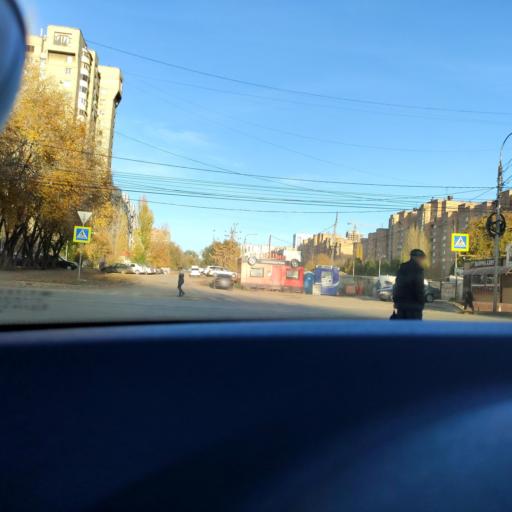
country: RU
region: Samara
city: Samara
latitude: 53.1933
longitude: 50.1392
